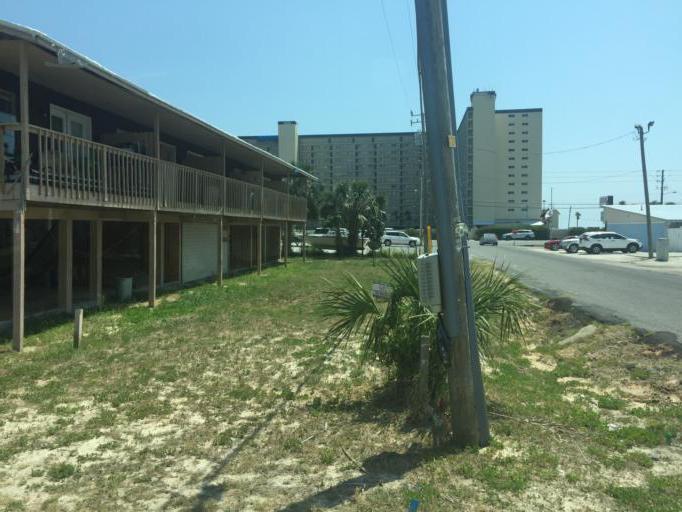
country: US
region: Florida
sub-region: Bay County
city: Lower Grand Lagoon
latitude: 30.1484
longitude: -85.7604
